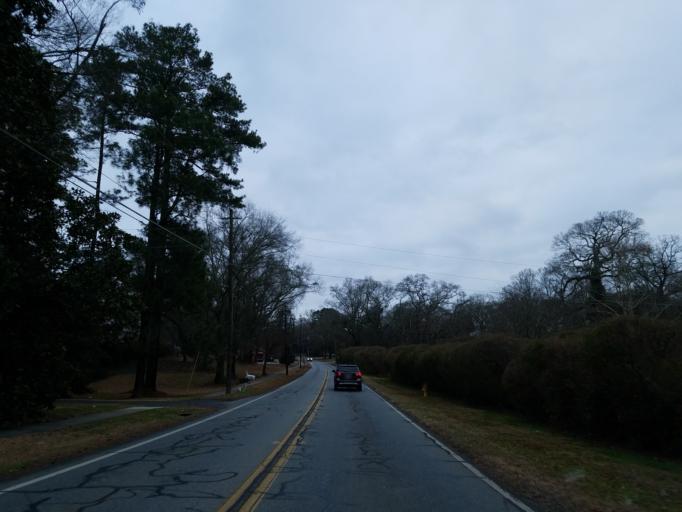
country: US
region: Georgia
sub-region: Bartow County
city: Cartersville
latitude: 34.1707
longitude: -84.8080
